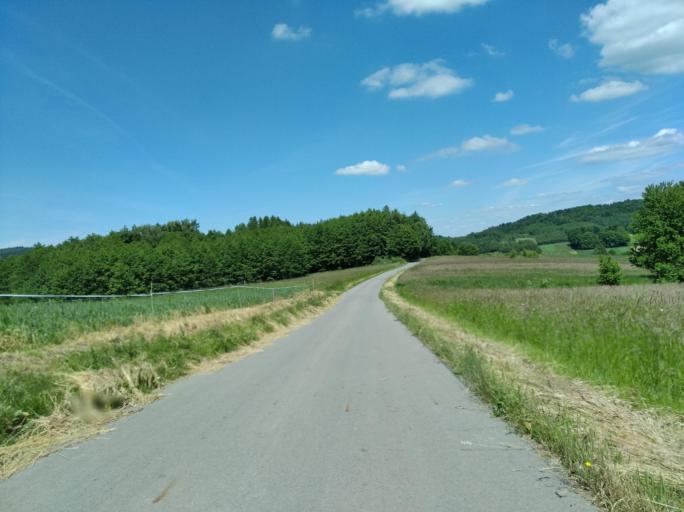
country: PL
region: Subcarpathian Voivodeship
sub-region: Powiat krosnienski
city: Wojaszowka
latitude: 49.7880
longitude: 21.7172
